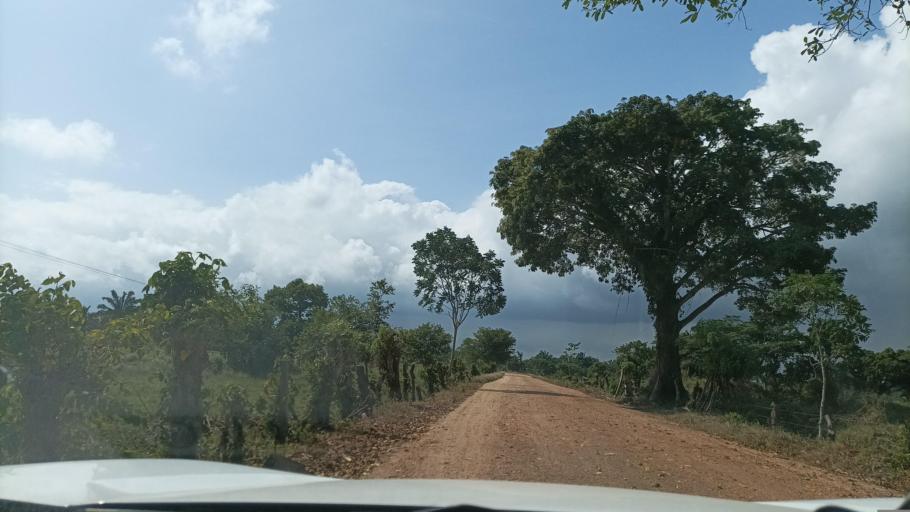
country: MX
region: Veracruz
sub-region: Chinameca
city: Chacalapa
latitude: 18.1346
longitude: -94.6533
